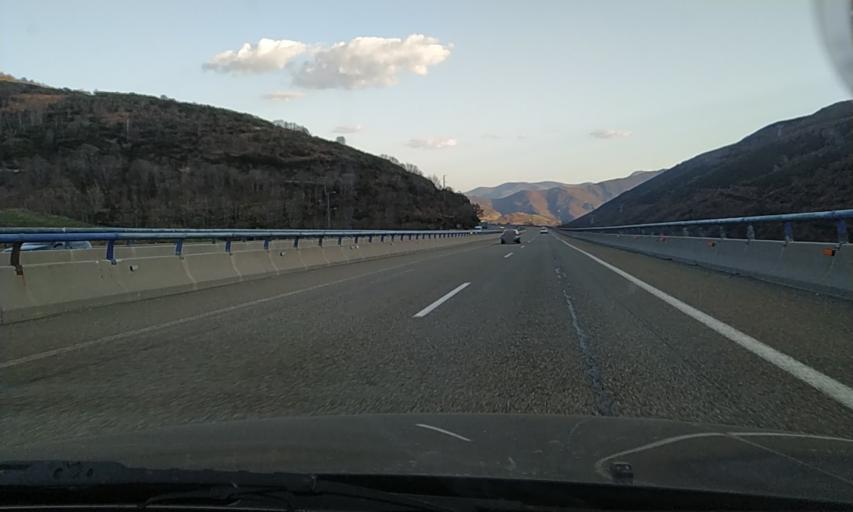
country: ES
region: Castille and Leon
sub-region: Provincia de Leon
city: Balboa
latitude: 42.7110
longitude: -7.0097
